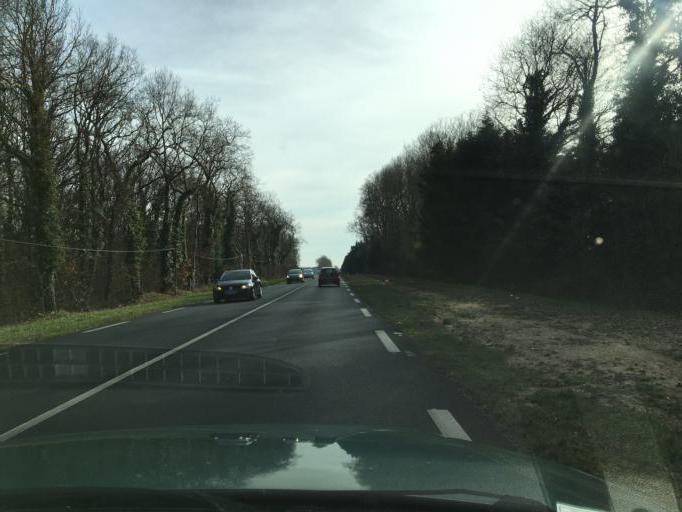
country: FR
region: Centre
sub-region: Departement du Loiret
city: Saint-Cyr-en-Val
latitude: 47.8087
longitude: 1.9294
